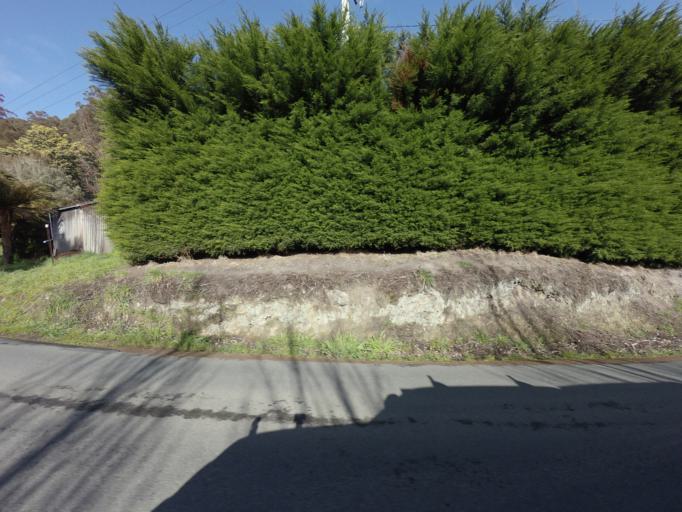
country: AU
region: Tasmania
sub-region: Huon Valley
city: Geeveston
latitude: -43.2476
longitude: 146.9909
